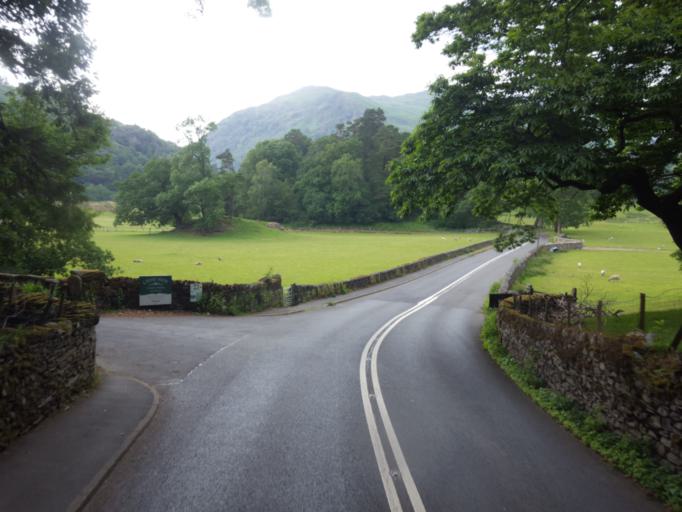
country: GB
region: England
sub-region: Cumbria
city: Ambleside
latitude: 54.4391
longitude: -2.9717
